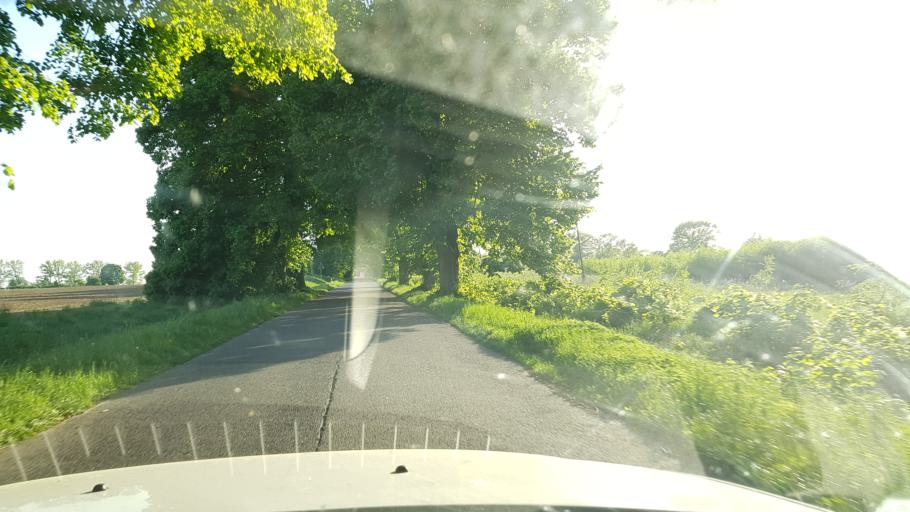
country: PL
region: West Pomeranian Voivodeship
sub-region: Powiat lobeski
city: Dobra
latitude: 53.5676
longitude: 15.2030
